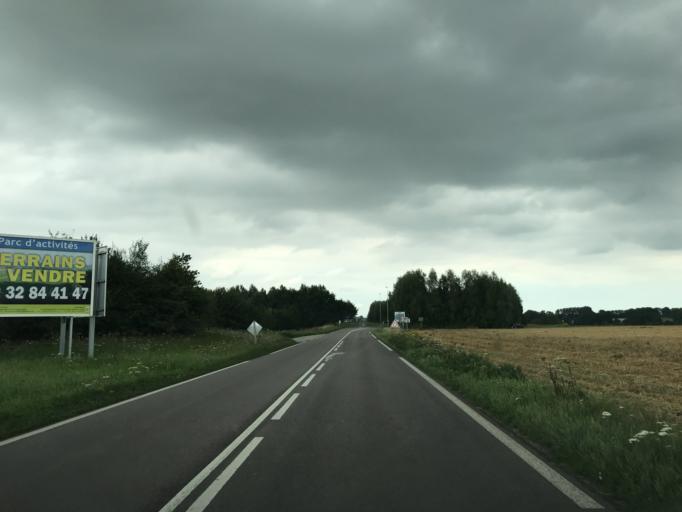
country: FR
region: Haute-Normandie
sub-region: Departement de la Seine-Maritime
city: Bolbec
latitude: 49.5807
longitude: 0.4495
